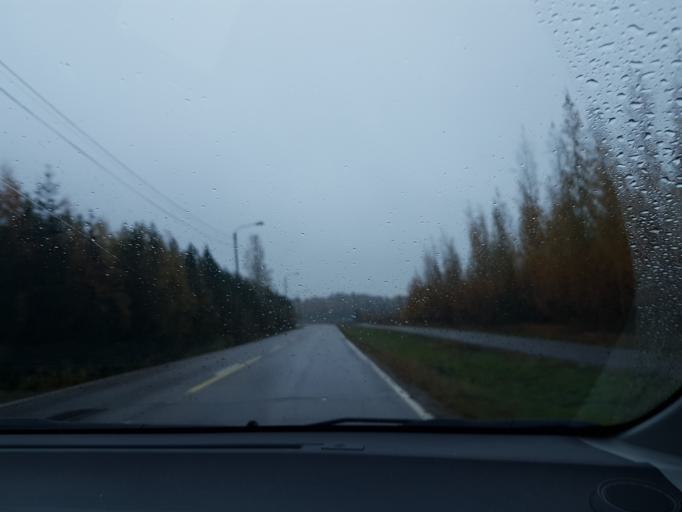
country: FI
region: Uusimaa
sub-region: Helsinki
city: Jaervenpaeae
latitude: 60.5518
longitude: 25.1260
